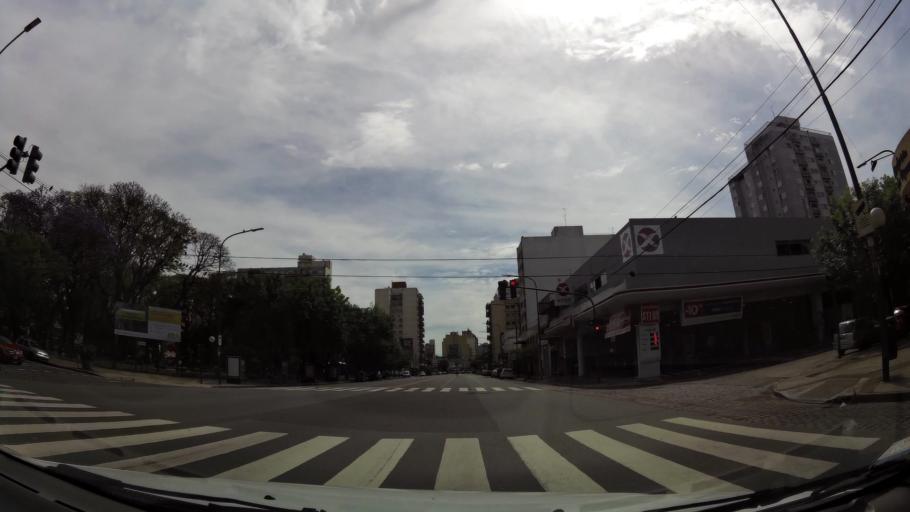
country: AR
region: Buenos Aires F.D.
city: Villa Santa Rita
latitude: -34.6388
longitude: -58.5086
